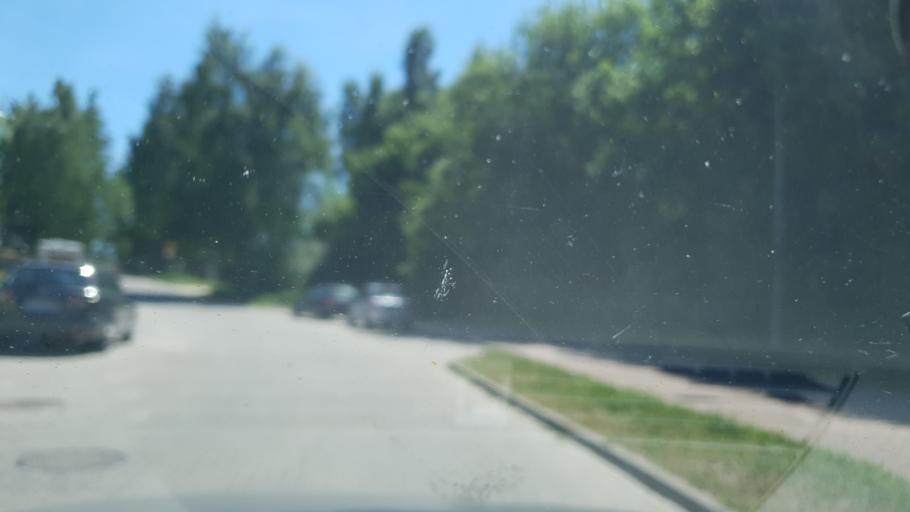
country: PL
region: Pomeranian Voivodeship
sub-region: Gdynia
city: Wielki Kack
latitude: 54.4685
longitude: 18.4812
